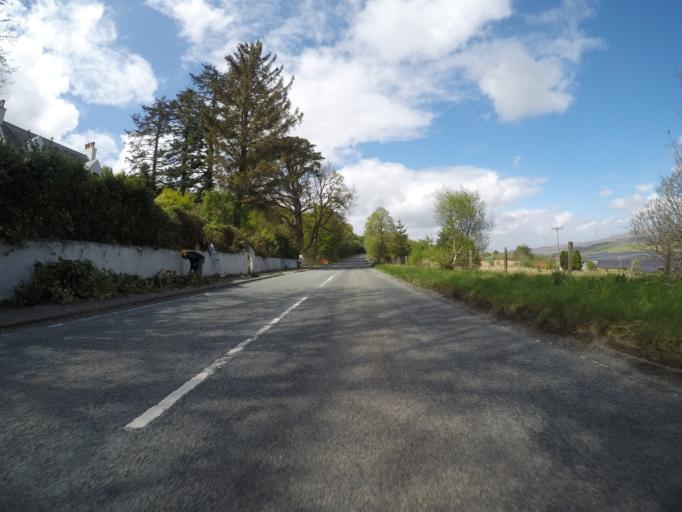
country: GB
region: Scotland
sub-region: Highland
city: Isle of Skye
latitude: 57.4578
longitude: -6.3269
